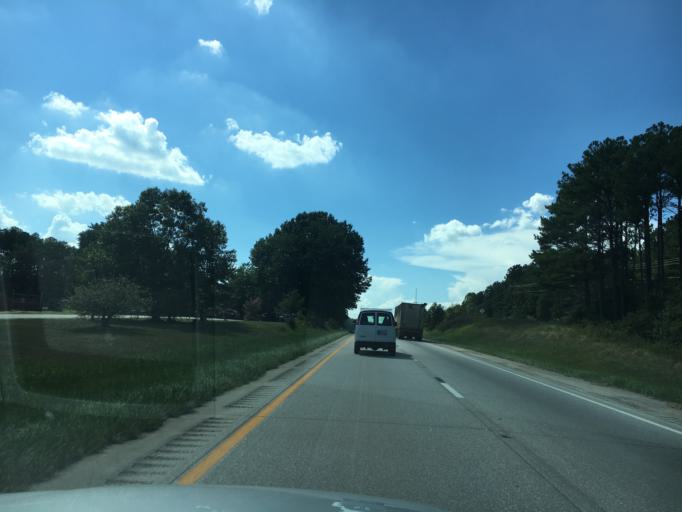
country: US
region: South Carolina
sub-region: Laurens County
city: Watts Mills
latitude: 34.5425
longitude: -81.9669
